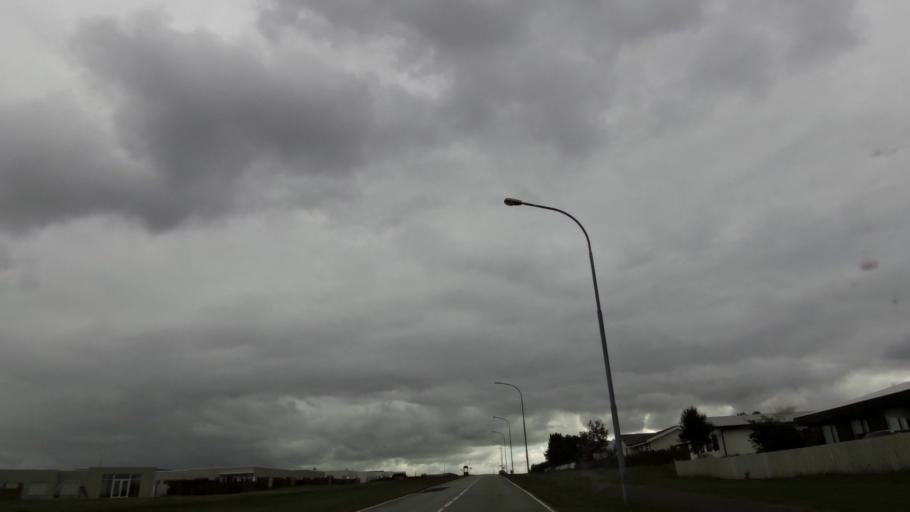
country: IS
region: Capital Region
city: Alftanes
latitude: 64.1036
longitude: -22.0271
